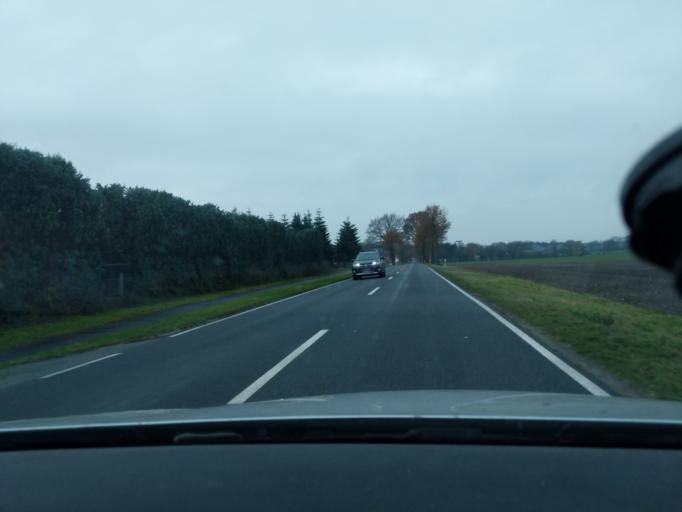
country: DE
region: Lower Saxony
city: Heeslingen
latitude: 53.3263
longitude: 9.3528
